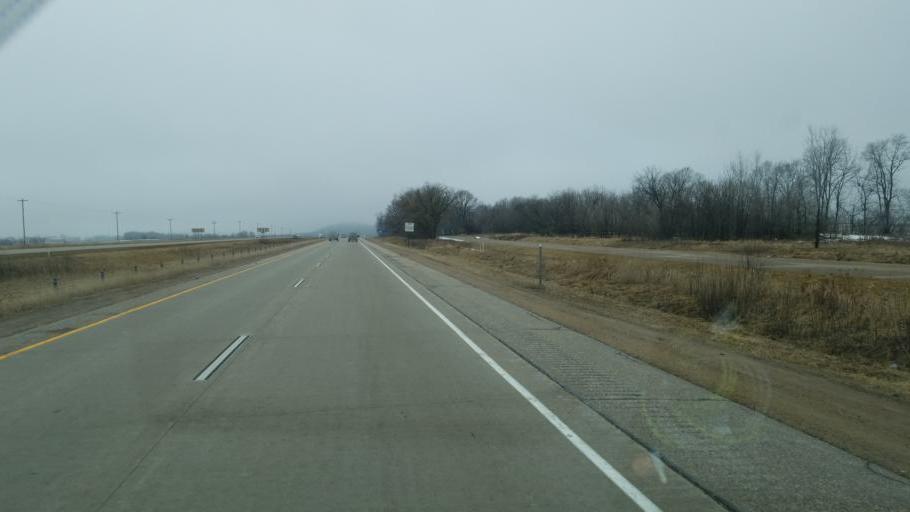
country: US
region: Wisconsin
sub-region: Waupaca County
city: Waupaca
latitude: 44.3295
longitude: -89.0249
